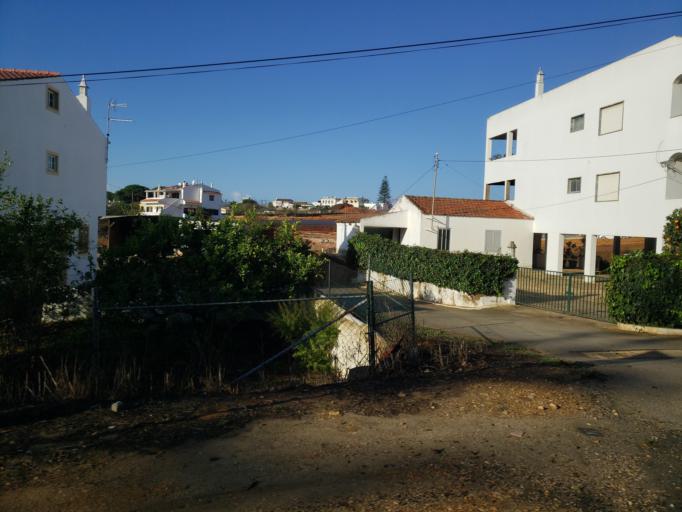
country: PT
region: Faro
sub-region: Portimao
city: Portimao
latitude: 37.1555
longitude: -8.5605
